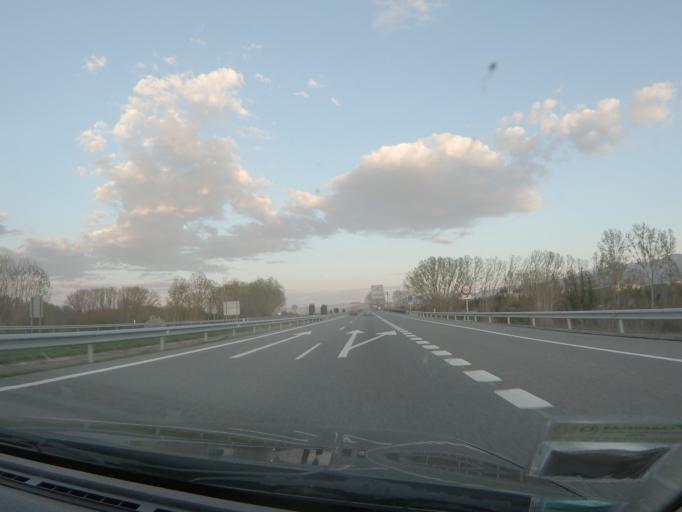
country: ES
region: Castille and Leon
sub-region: Provincia de Leon
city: Carracedelo
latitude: 42.5675
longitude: -6.7324
